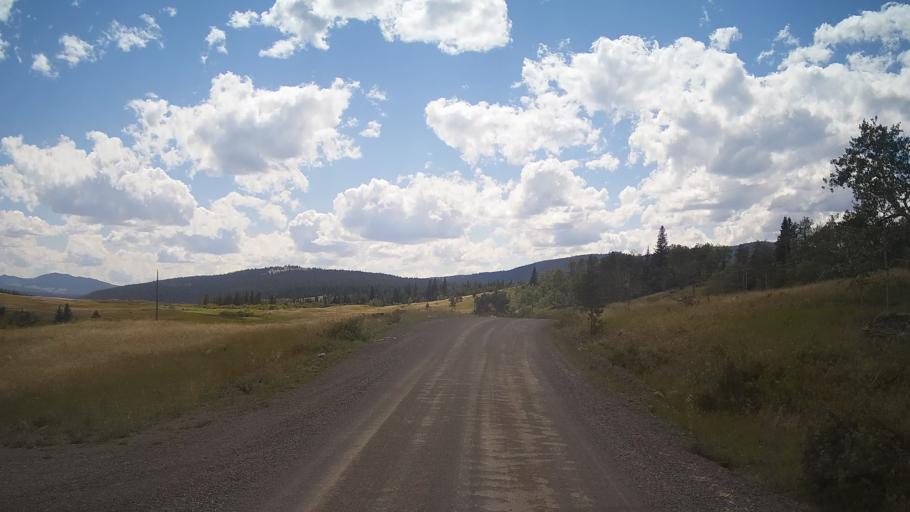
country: CA
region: British Columbia
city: Lillooet
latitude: 51.3273
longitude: -121.9773
